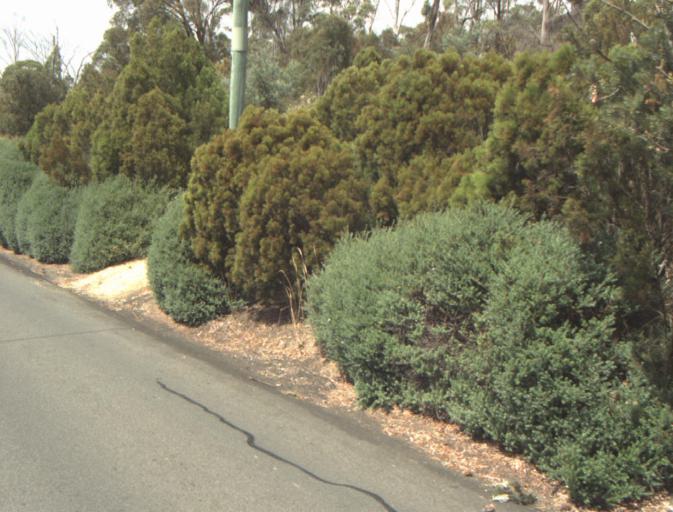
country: AU
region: Tasmania
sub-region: Launceston
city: Newstead
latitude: -41.4666
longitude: 147.1759
